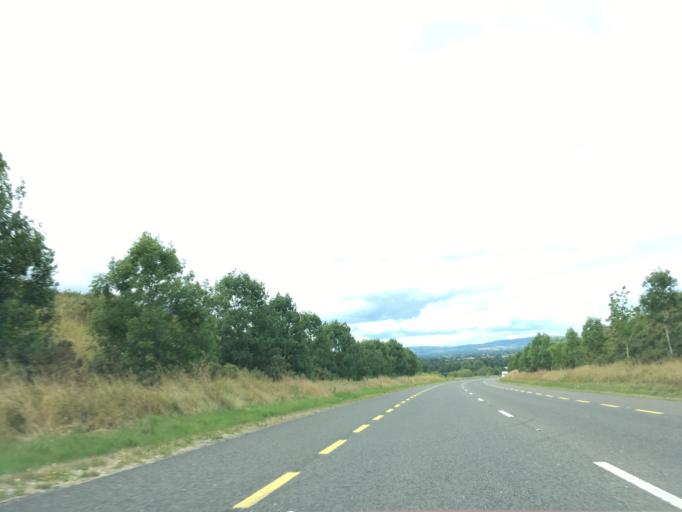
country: IE
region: Munster
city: Cashel
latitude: 52.5060
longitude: -7.9039
